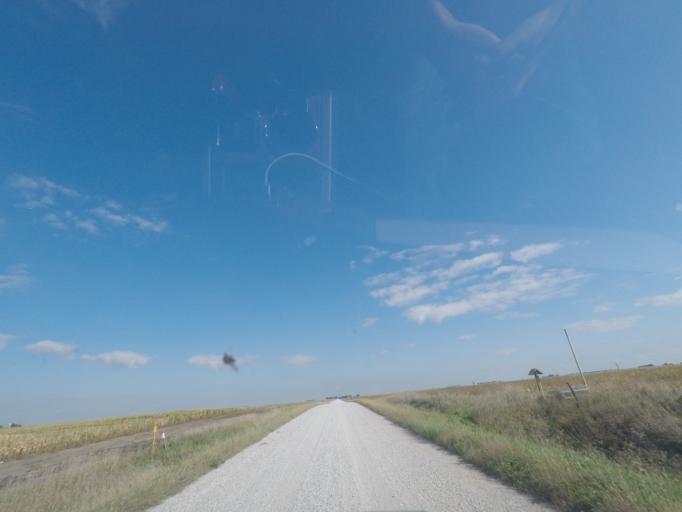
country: US
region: Iowa
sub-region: Story County
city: Nevada
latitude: 42.0384
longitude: -93.4252
